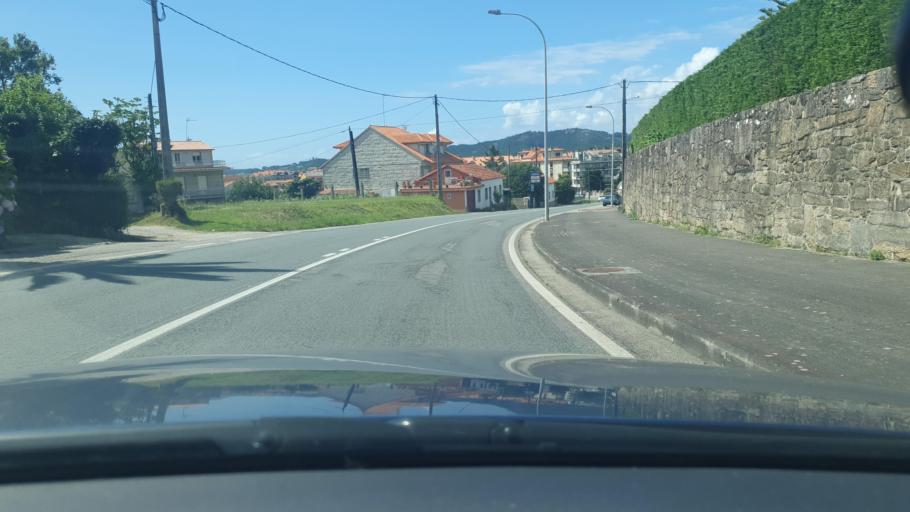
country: ES
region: Galicia
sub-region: Provincia de Pontevedra
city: O Grove
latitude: 42.4429
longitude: -8.8563
